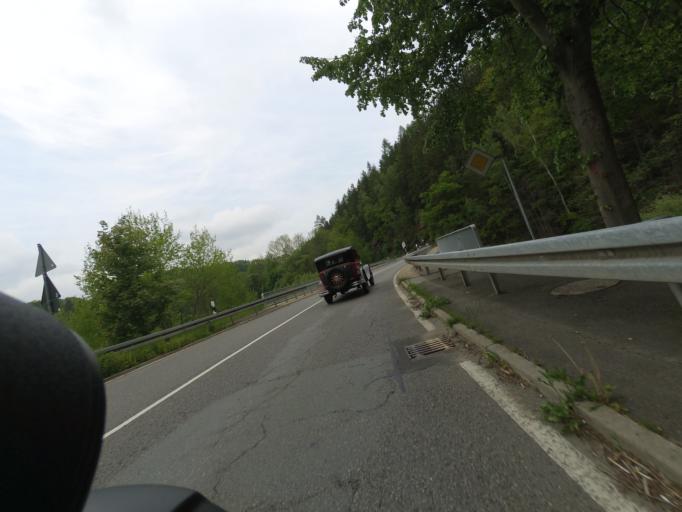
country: DE
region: Saxony
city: Scharfenstein
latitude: 50.7092
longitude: 13.0563
